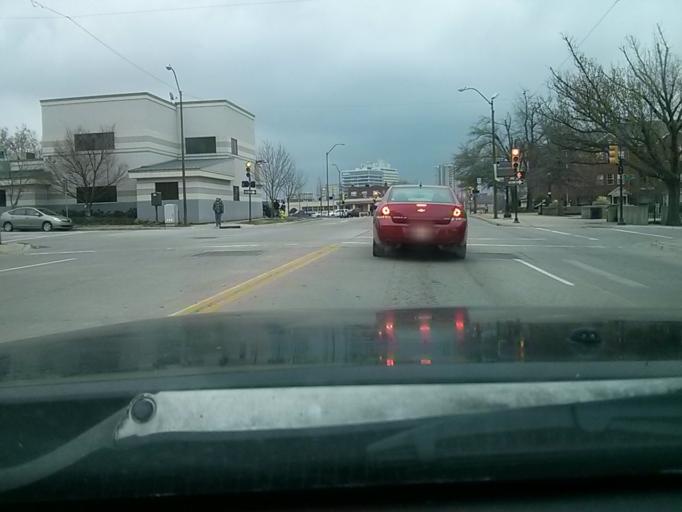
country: US
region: Oklahoma
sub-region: Tulsa County
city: Tulsa
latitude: 36.1486
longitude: -95.9927
